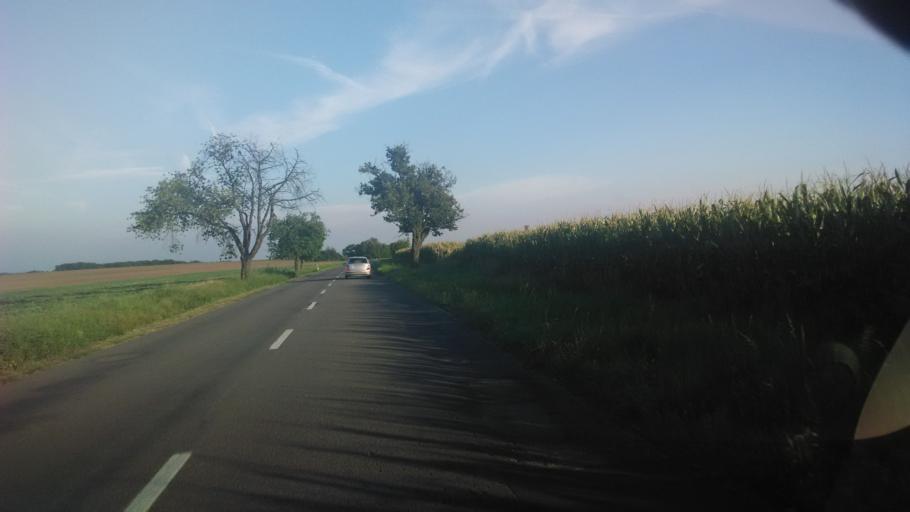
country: SK
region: Banskobystricky
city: Dudince
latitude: 48.2291
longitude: 18.7618
